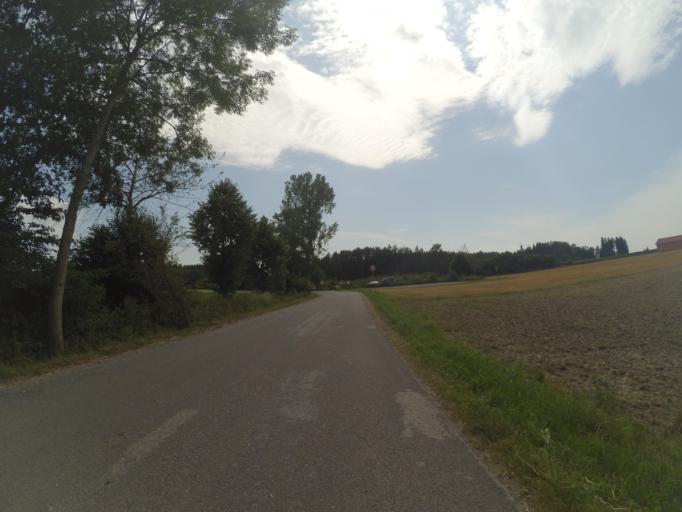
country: DE
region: Bavaria
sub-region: Swabia
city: Buchloe
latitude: 48.0307
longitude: 10.7404
